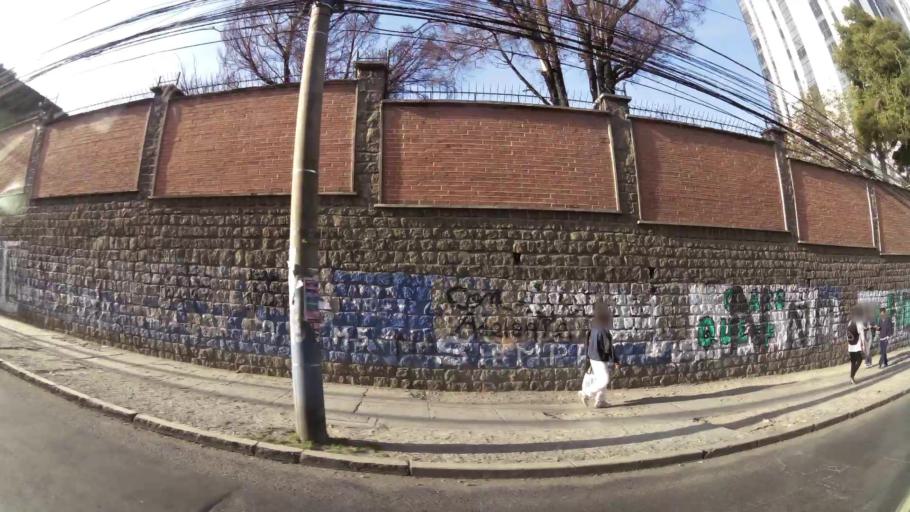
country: BO
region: La Paz
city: La Paz
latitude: -16.5298
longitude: -68.1015
